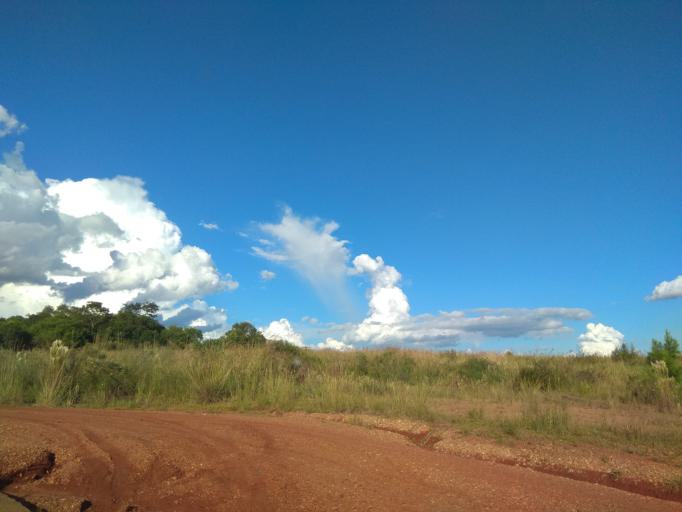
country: AR
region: Misiones
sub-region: Departamento de Candelaria
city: Candelaria
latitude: -27.4894
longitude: -55.7581
